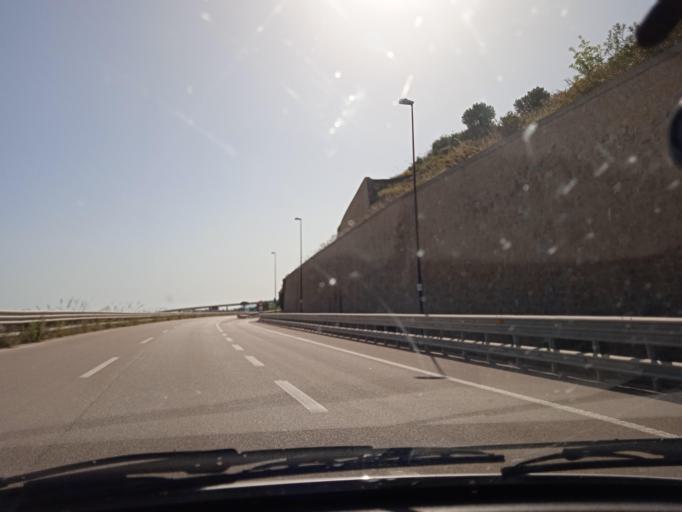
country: IT
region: Sicily
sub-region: Messina
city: Motta d'Affermo
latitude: 38.0057
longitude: 14.3199
